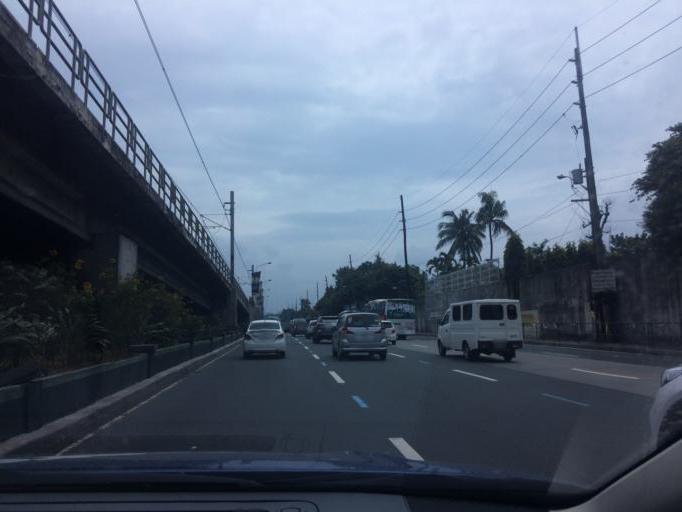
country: PH
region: Metro Manila
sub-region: Makati City
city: Makati City
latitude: 14.5425
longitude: 121.0202
